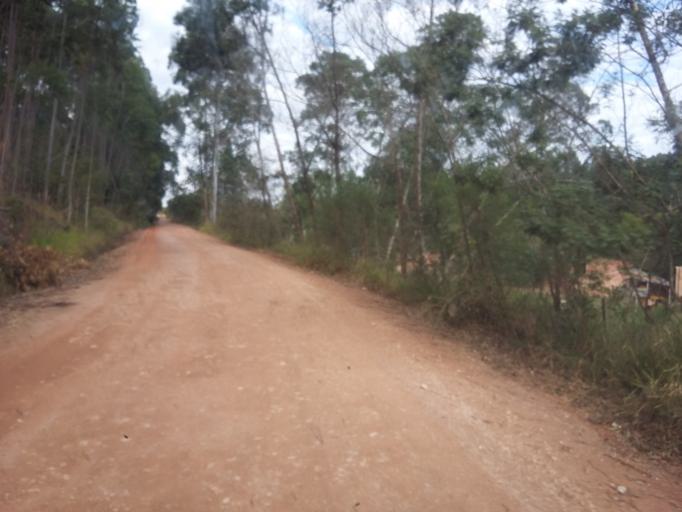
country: BR
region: Rio Grande do Sul
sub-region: Camaqua
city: Camaqua
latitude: -30.7219
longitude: -51.7830
